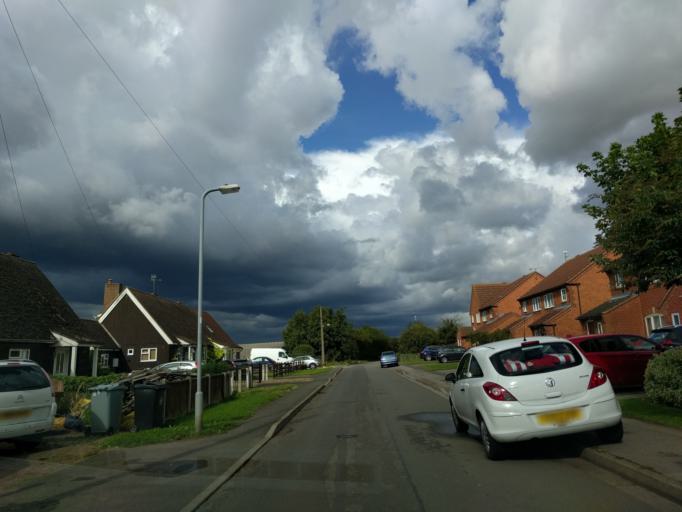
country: GB
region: England
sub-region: Lincolnshire
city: Long Bennington
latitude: 53.0339
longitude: -0.7356
